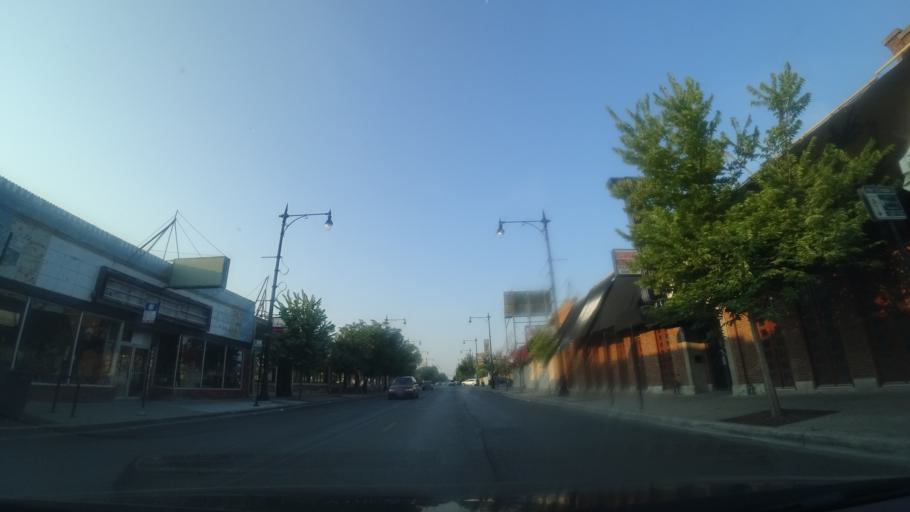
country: US
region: Illinois
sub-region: Cook County
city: Elmwood Park
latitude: 41.9377
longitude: -87.7665
